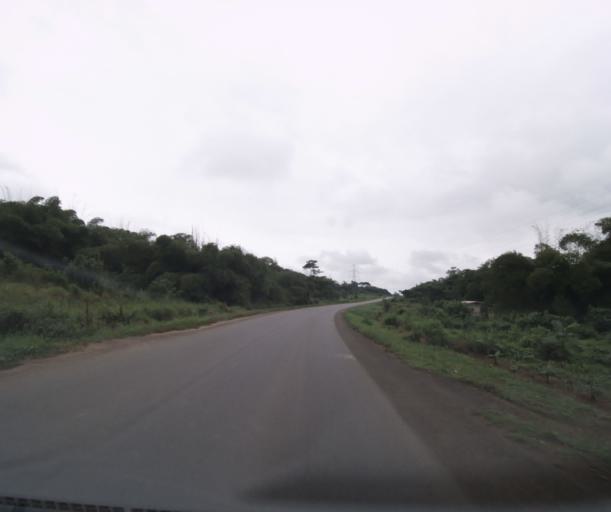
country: CM
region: Littoral
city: Edea
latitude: 3.7400
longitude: 10.1175
